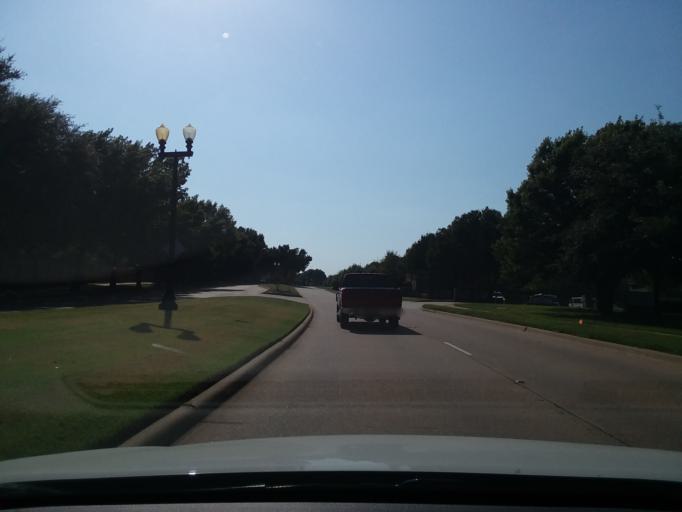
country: US
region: Texas
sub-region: Denton County
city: Flower Mound
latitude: 33.0268
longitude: -97.0868
